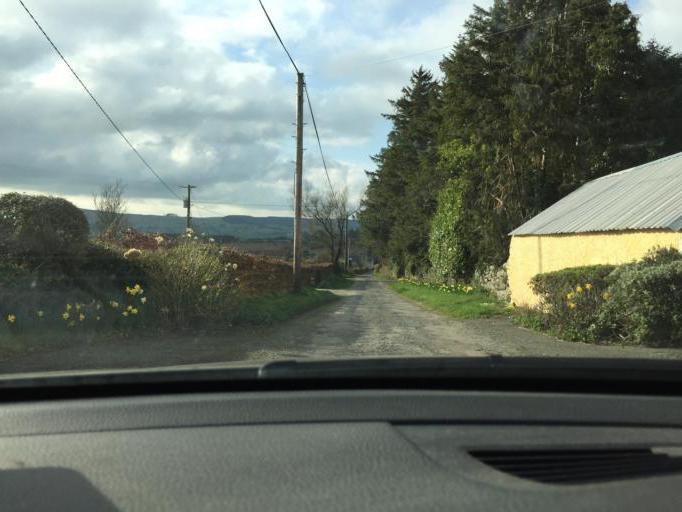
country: IE
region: Leinster
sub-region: Wicklow
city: Valleymount
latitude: 53.0811
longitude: -6.5151
